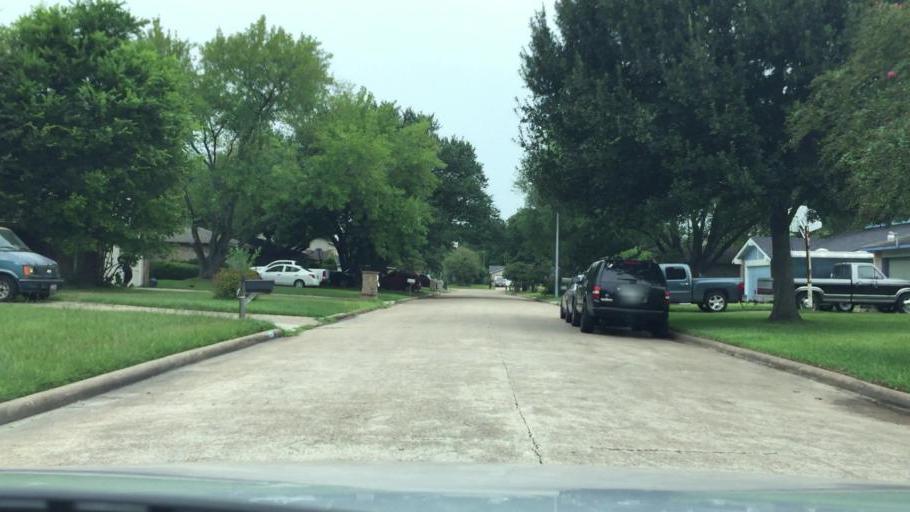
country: US
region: Texas
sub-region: Harris County
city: Hudson
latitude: 29.9056
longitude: -95.5139
